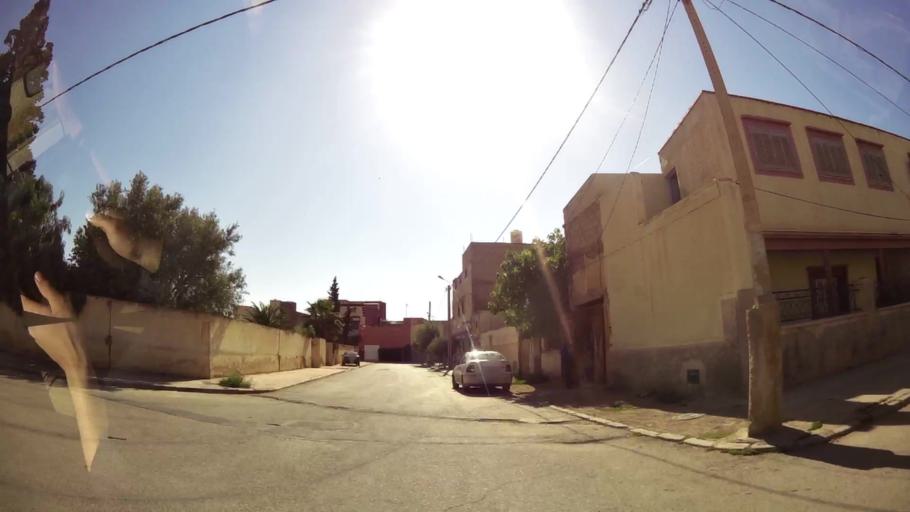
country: MA
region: Oriental
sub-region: Oujda-Angad
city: Oujda
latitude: 34.6877
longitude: -1.9220
